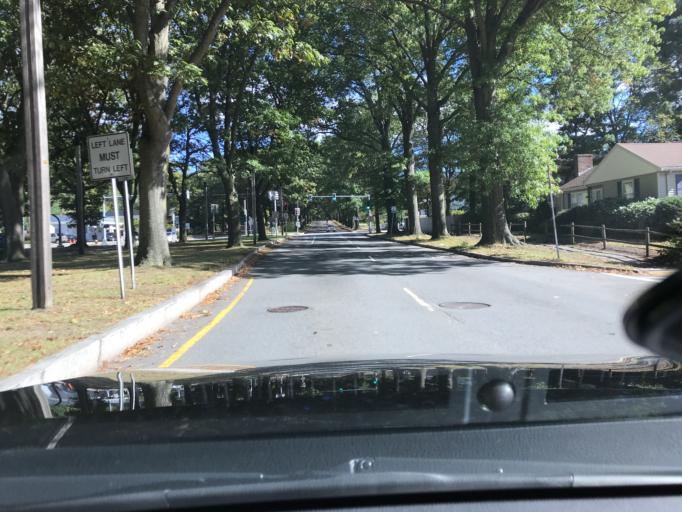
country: US
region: Massachusetts
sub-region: Suffolk County
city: Jamaica Plain
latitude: 42.2927
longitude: -71.1637
